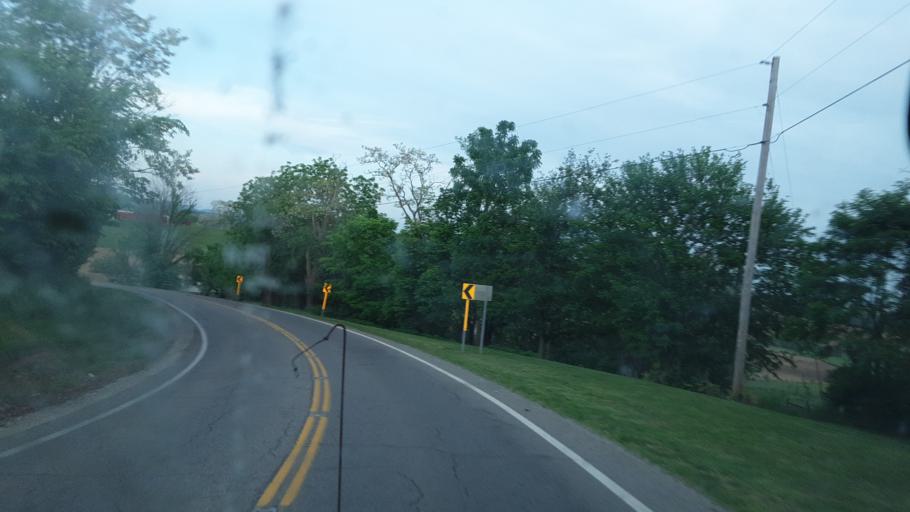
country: US
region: Ohio
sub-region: Ross County
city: Kingston
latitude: 39.4614
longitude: -82.7631
